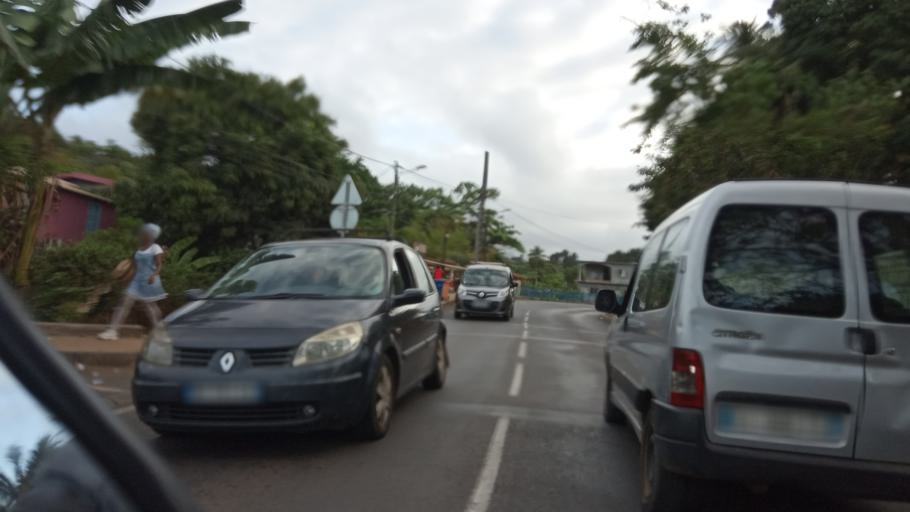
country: YT
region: Dembeni
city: Dembeni
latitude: -12.8151
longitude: 45.2004
